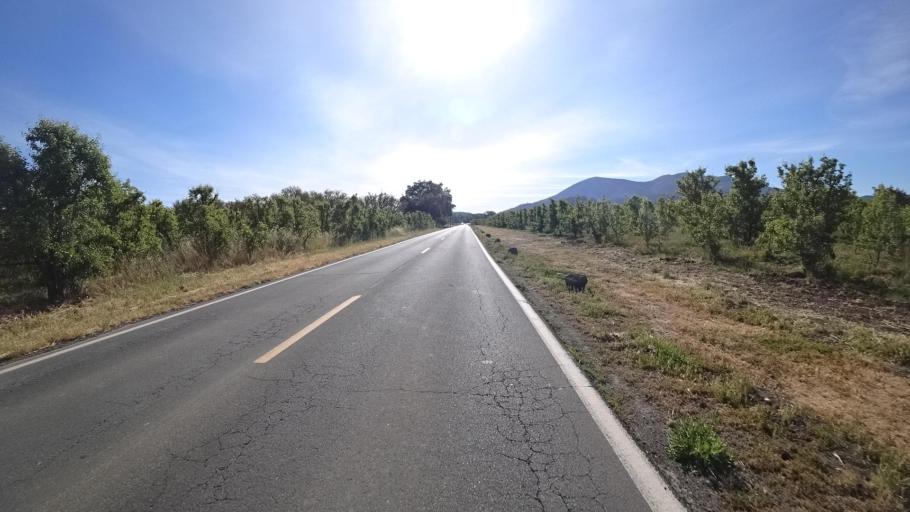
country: US
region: California
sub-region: Lake County
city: Kelseyville
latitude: 39.0112
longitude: -122.8444
